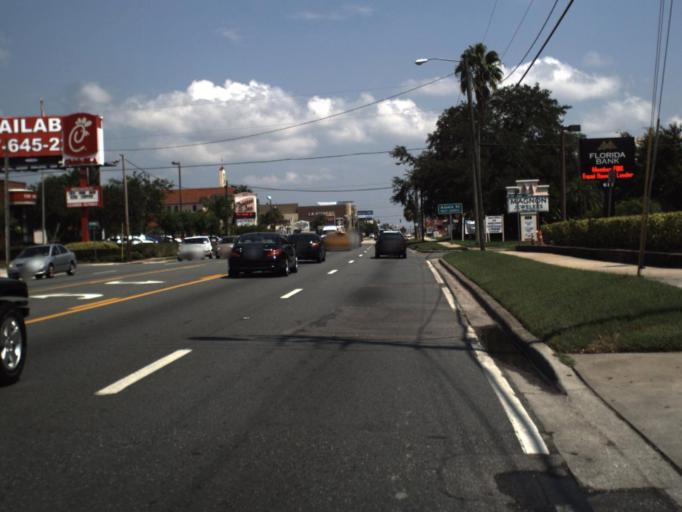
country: US
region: Florida
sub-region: Hillsborough County
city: Tampa
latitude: 27.9380
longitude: -82.5057
